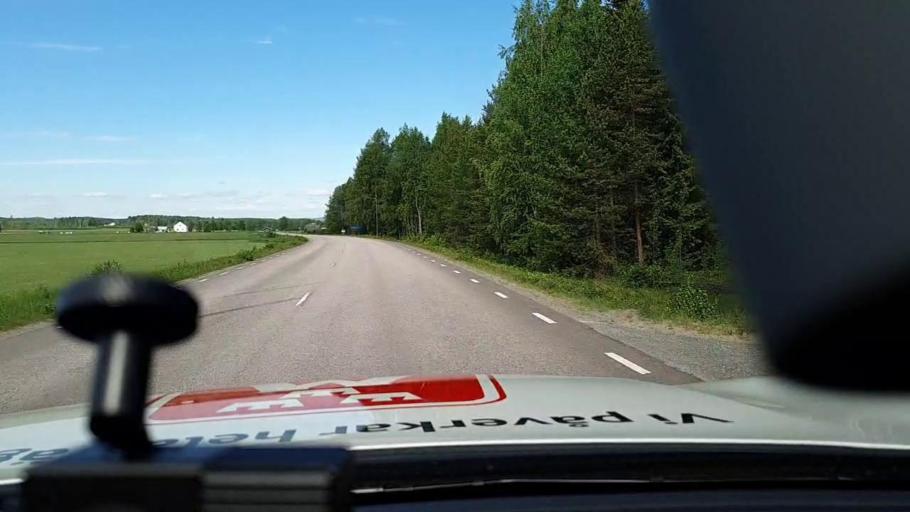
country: SE
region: Norrbotten
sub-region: Lulea Kommun
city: Sodra Sunderbyn
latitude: 65.6479
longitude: 21.8787
